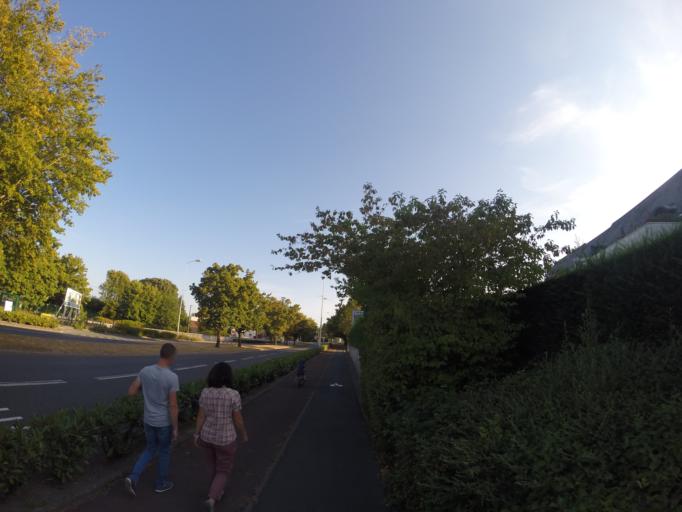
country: FR
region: Centre
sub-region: Departement d'Indre-et-Loire
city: Tours
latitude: 47.4155
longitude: 0.7032
